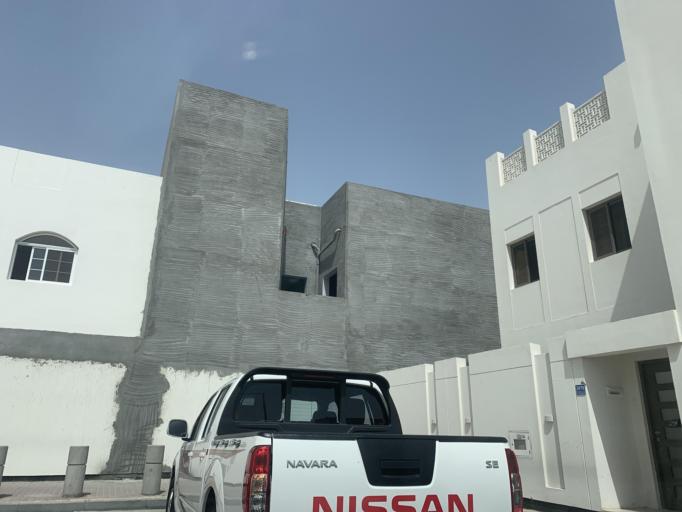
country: BH
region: Northern
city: Ar Rifa'
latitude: 26.1491
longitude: 50.5644
